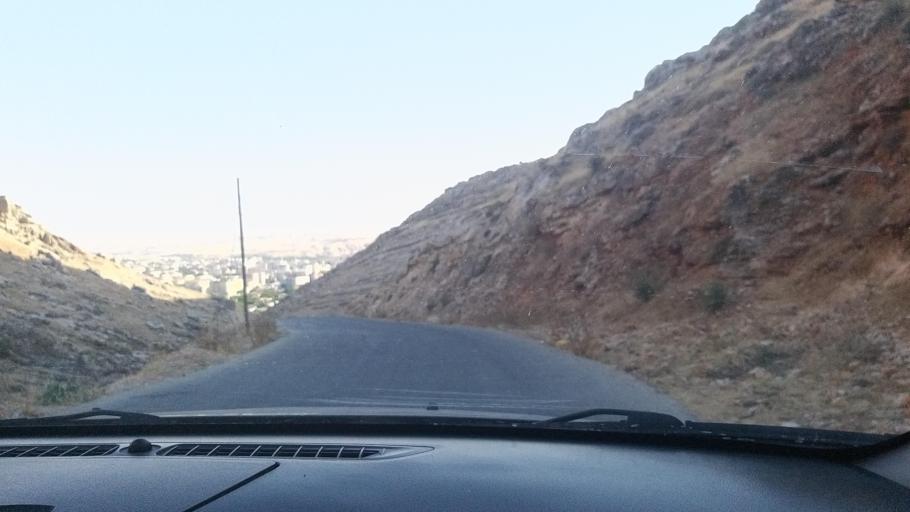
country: TR
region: Diyarbakir
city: Silvan
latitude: 38.1593
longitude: 41.0029
